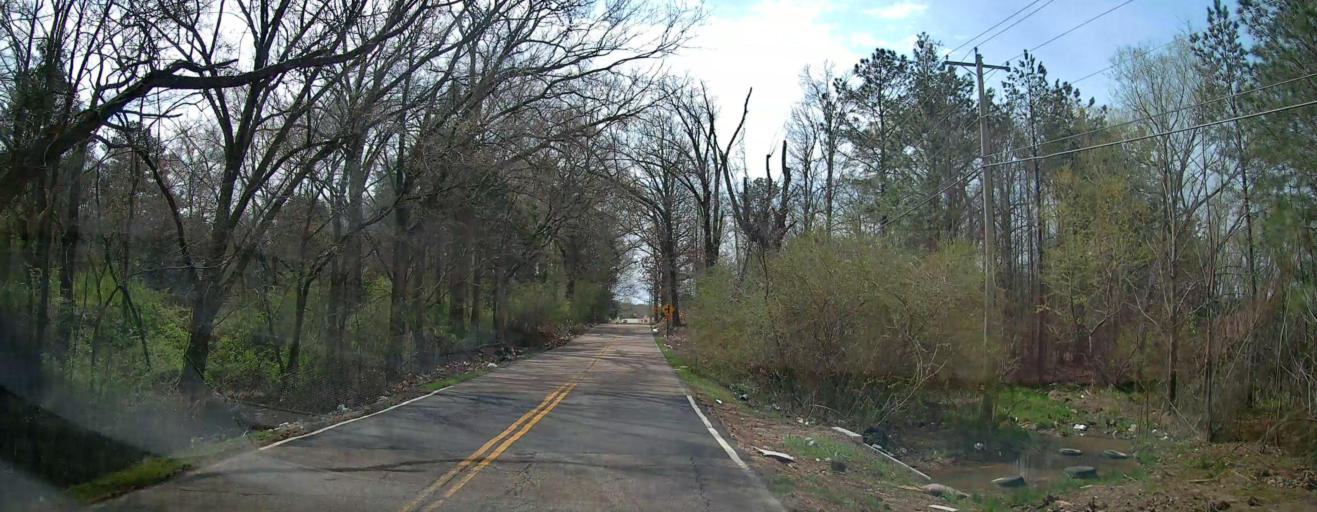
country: US
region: Mississippi
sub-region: De Soto County
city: Olive Branch
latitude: 34.9965
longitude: -89.8484
